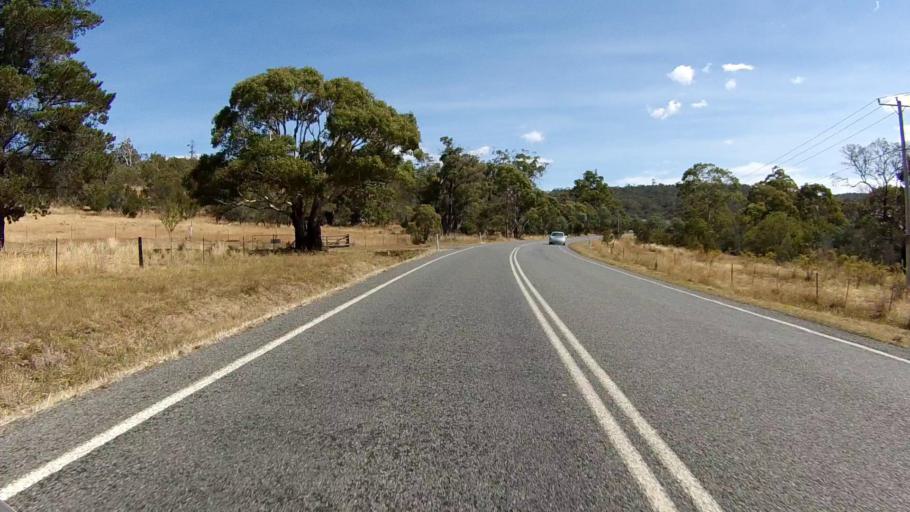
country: AU
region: Tasmania
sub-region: Sorell
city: Sorell
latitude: -42.6070
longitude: 147.6980
